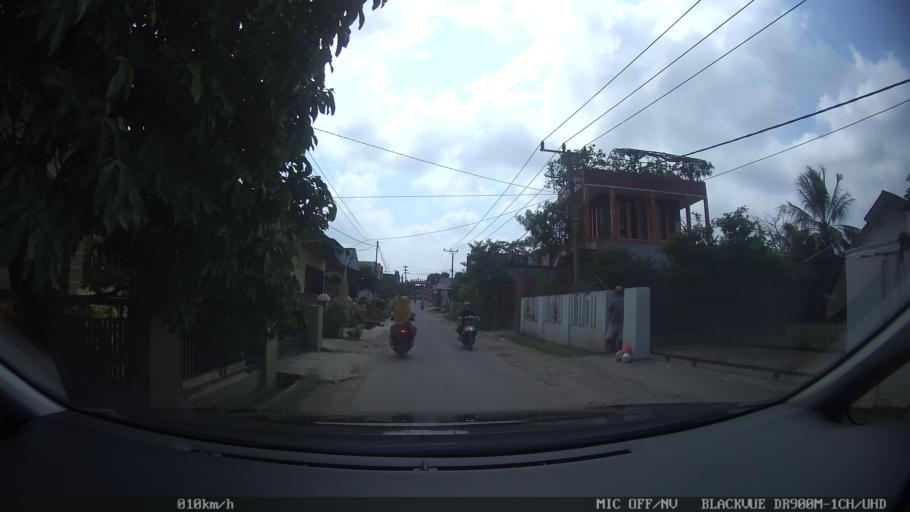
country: ID
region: Lampung
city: Kedaton
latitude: -5.3419
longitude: 105.2929
